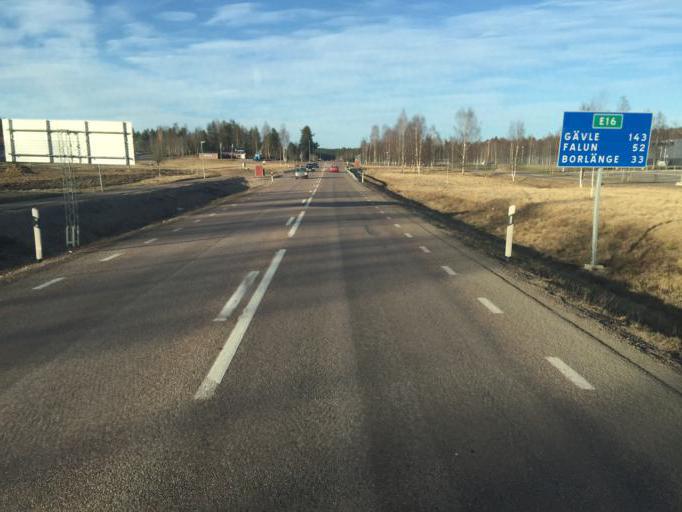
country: SE
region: Dalarna
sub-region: Gagnefs Kommun
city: Mockfjard
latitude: 60.5089
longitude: 14.9635
